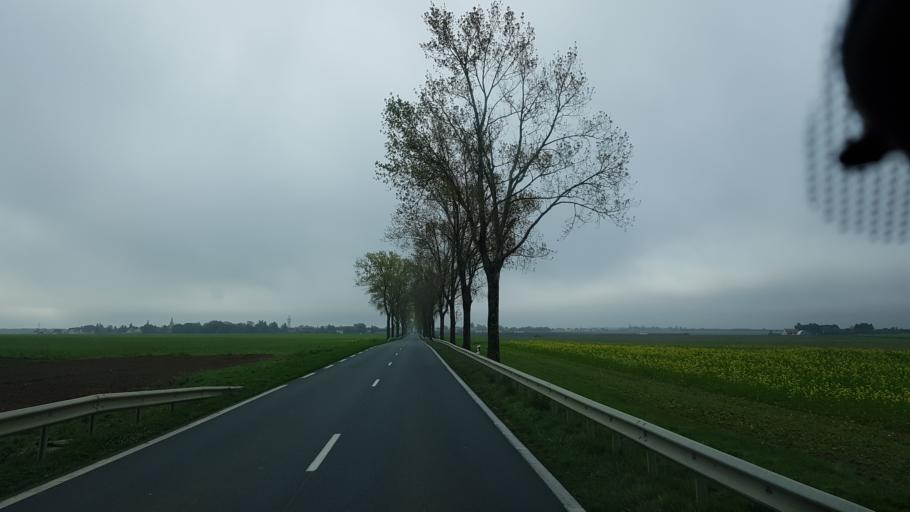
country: FR
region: Ile-de-France
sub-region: Departement de l'Essonne
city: Corbreuse
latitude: 48.4407
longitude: 1.9582
